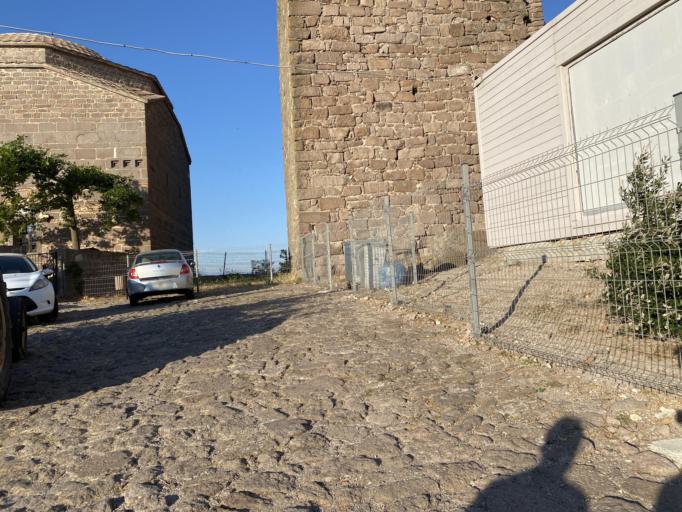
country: TR
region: Canakkale
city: Behram
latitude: 39.4918
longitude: 26.3366
